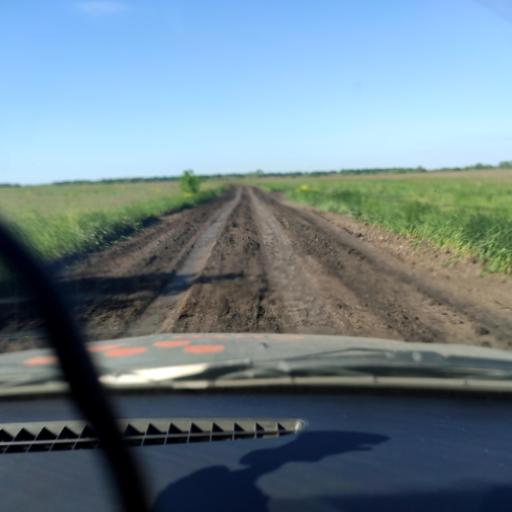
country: RU
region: Bashkortostan
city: Avdon
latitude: 54.5696
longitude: 55.8356
